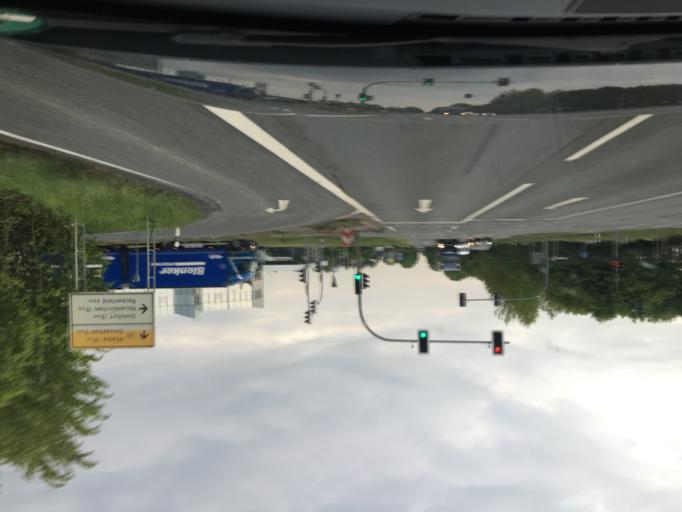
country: DE
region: North Rhine-Westphalia
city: Emsdetten
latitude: 52.1439
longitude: 7.5641
